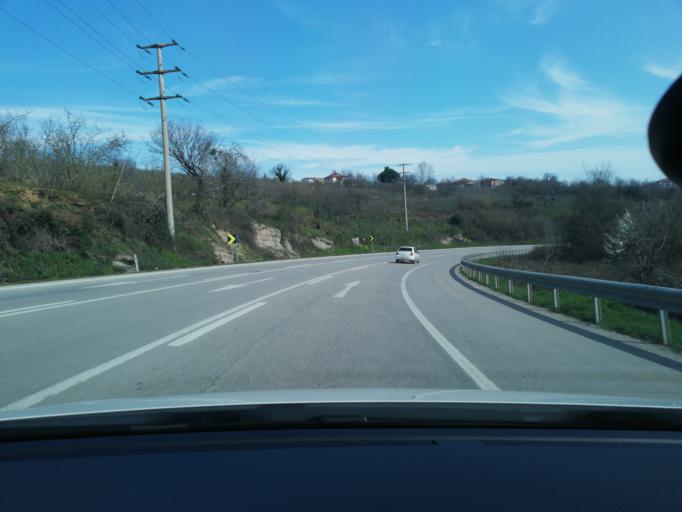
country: TR
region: Duzce
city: Akcakoca
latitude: 41.0772
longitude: 31.1128
